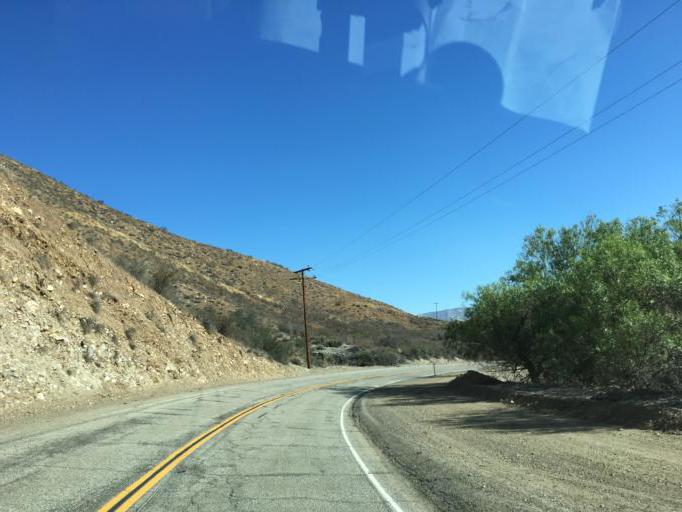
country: US
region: California
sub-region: Los Angeles County
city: Agua Dulce
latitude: 34.4482
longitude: -118.3342
